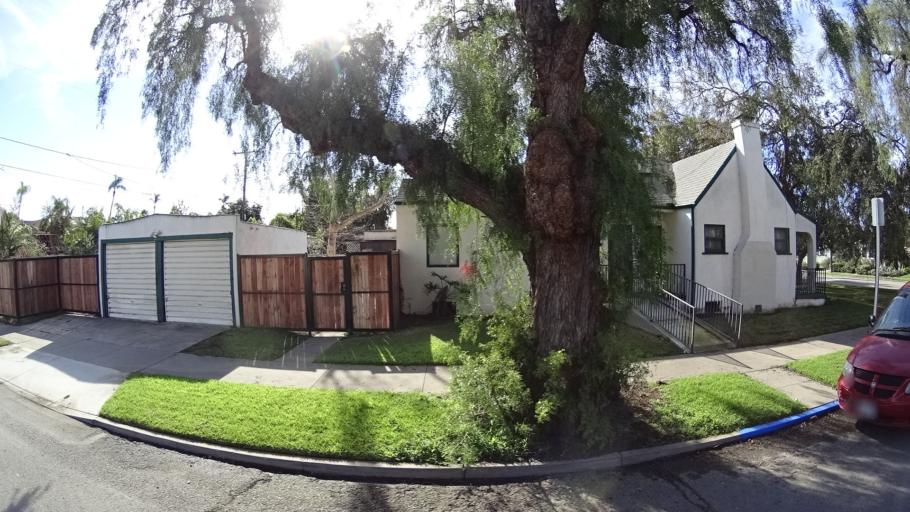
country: US
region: California
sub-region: Orange County
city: Santa Ana
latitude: 33.7327
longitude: -117.8731
